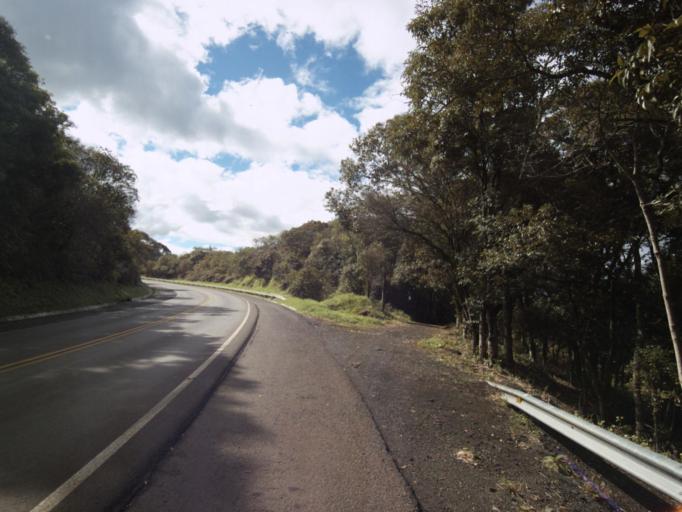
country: BR
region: Santa Catarina
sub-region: Concordia
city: Concordia
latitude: -27.3471
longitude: -51.9870
